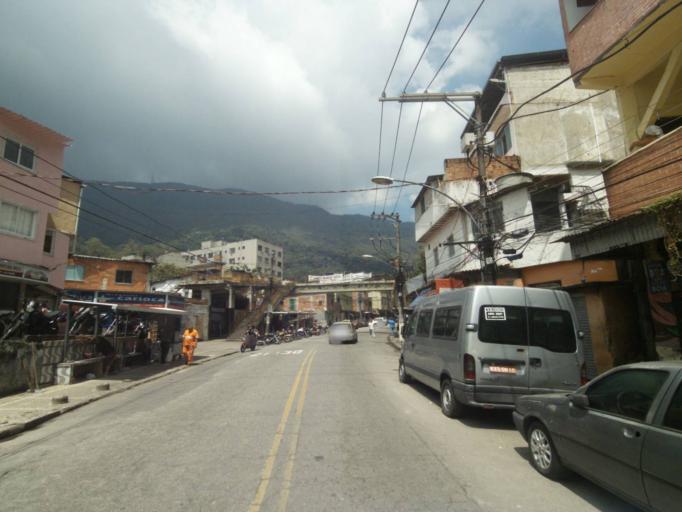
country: BR
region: Rio de Janeiro
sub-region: Rio De Janeiro
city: Rio de Janeiro
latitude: -22.9409
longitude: -43.2537
